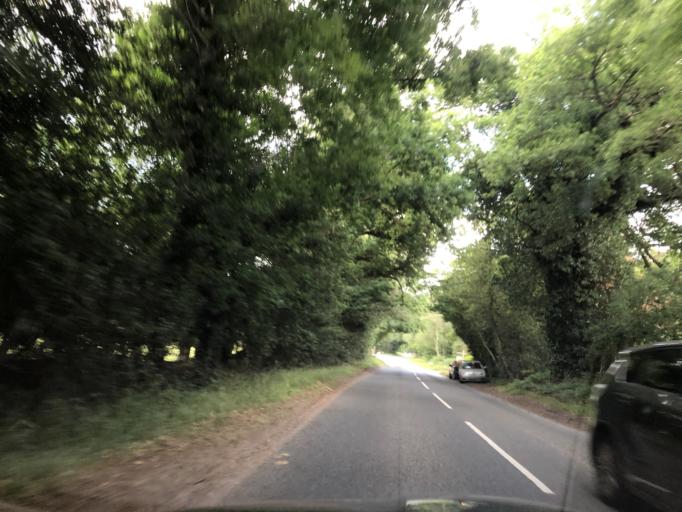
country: GB
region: England
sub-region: Hampshire
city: Eversley
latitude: 51.3466
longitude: -0.8895
